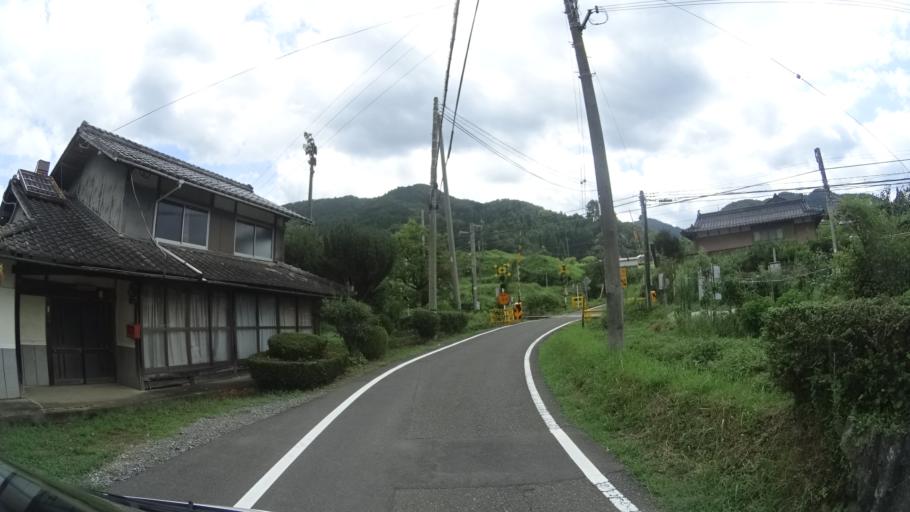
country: JP
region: Kyoto
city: Ayabe
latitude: 35.2711
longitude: 135.3498
